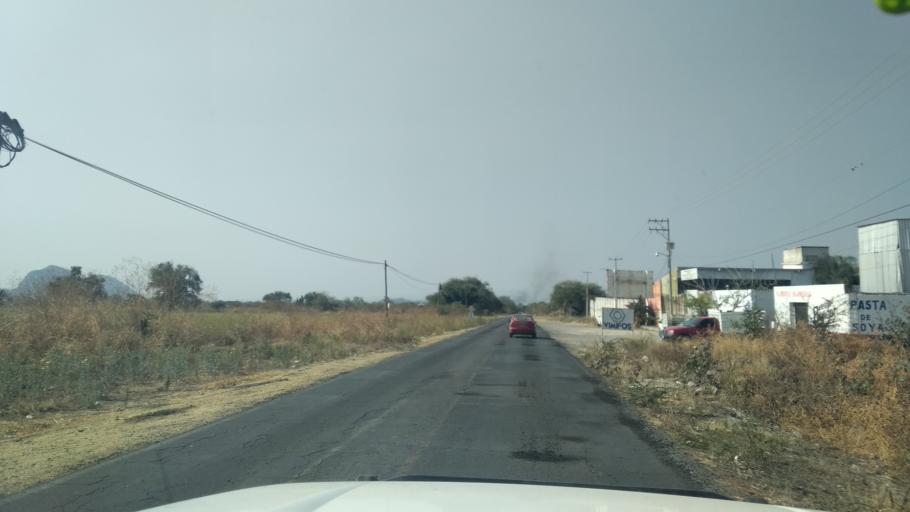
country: MX
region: Morelos
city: Amayuca
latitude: 18.7341
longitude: -98.7878
